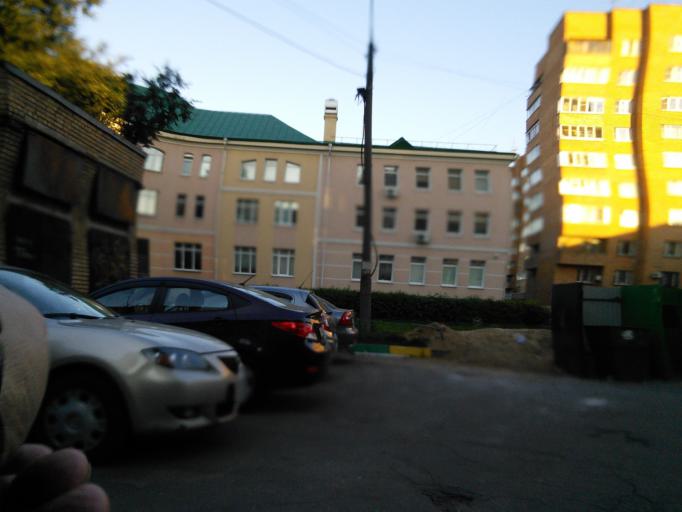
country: RU
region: Moskovskaya
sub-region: Podol'skiy Rayon
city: Podol'sk
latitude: 55.4318
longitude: 37.5475
